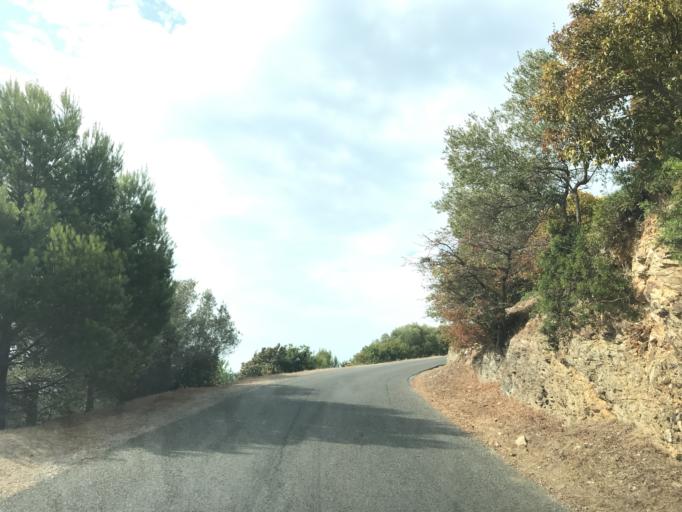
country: FR
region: Provence-Alpes-Cote d'Azur
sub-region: Departement du Var
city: Six-Fours-les-Plages
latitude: 43.1020
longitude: 5.8411
